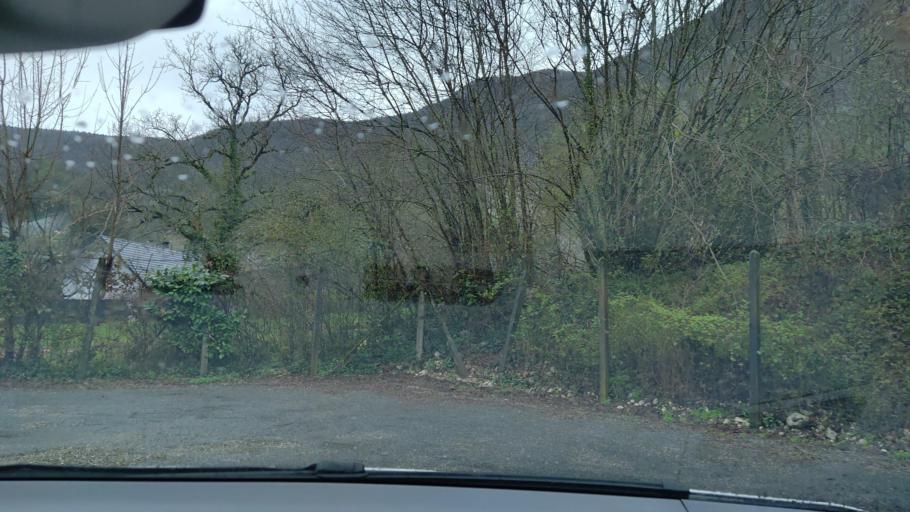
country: FR
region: Rhone-Alpes
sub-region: Departement de la Savoie
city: Vimines
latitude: 45.5368
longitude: 5.8156
